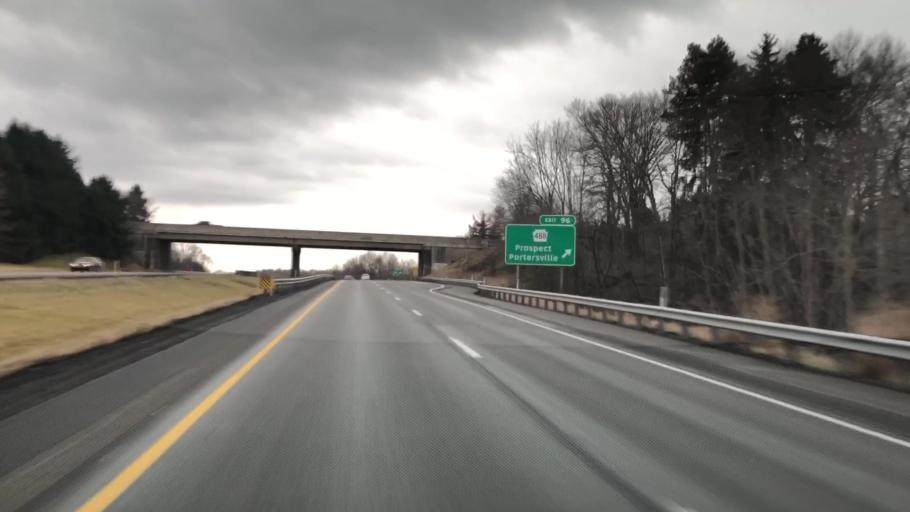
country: US
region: Pennsylvania
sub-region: Butler County
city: Prospect
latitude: 40.9230
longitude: -80.1330
